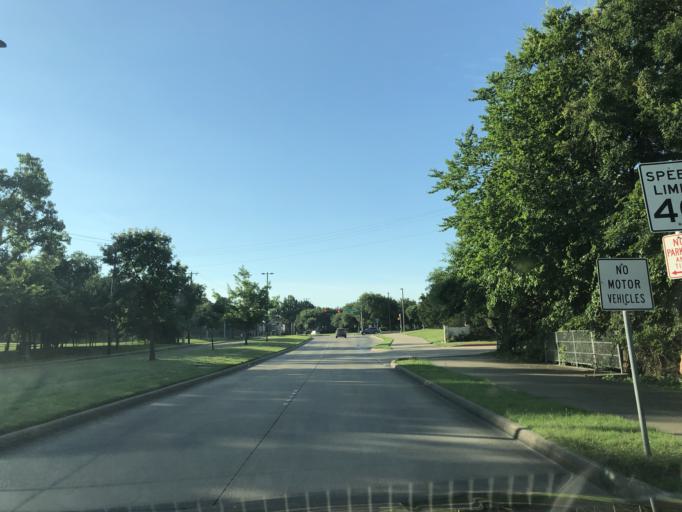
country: US
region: Texas
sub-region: Dallas County
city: Sunnyvale
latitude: 32.8463
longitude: -96.6023
